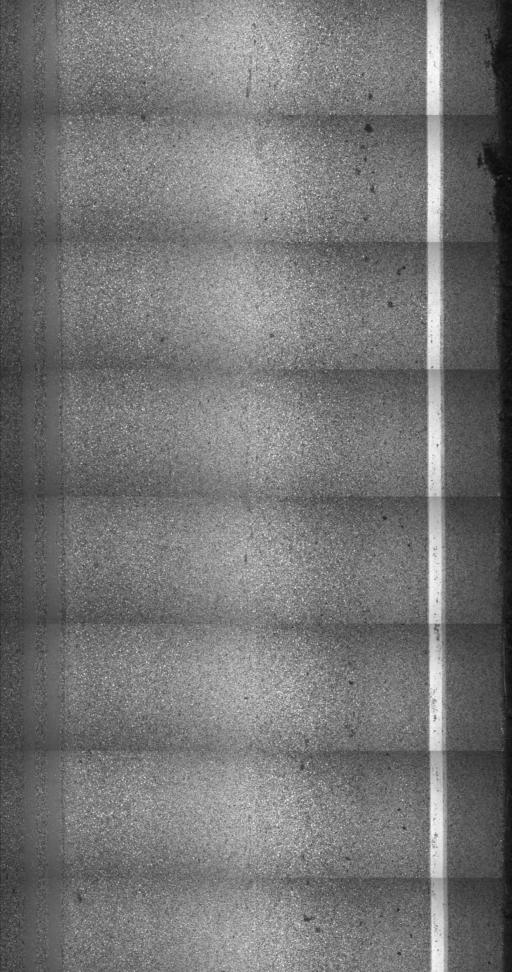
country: US
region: Vermont
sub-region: Rutland County
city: Poultney
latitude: 43.4366
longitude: -73.1116
